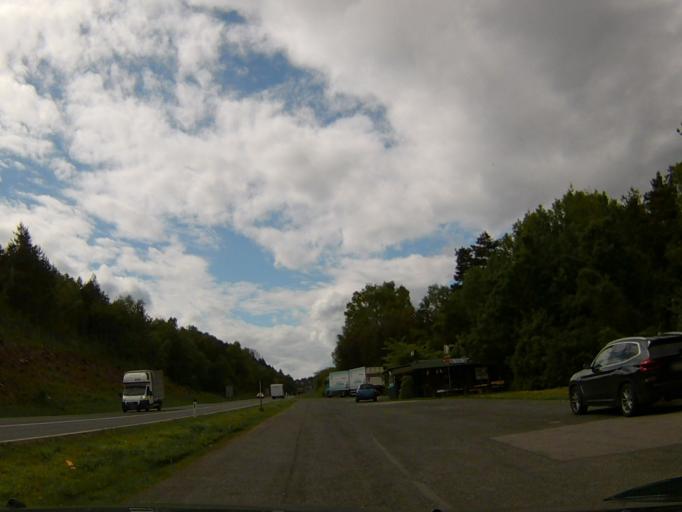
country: AT
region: Carinthia
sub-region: Villach Stadt
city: Villach
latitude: 46.6444
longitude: 13.7985
